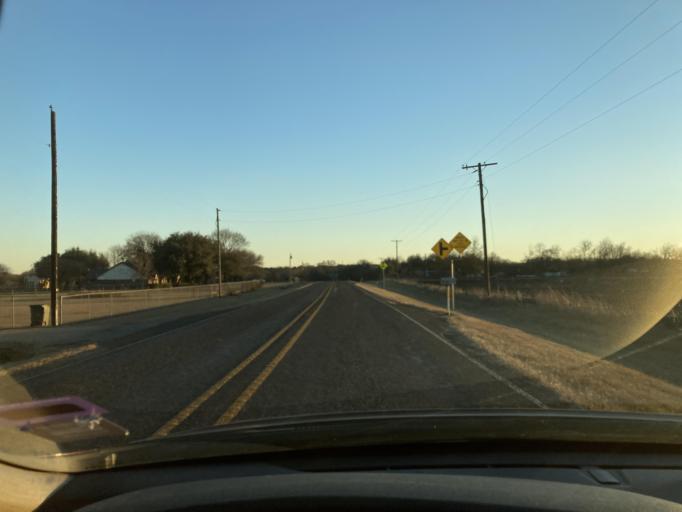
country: US
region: Texas
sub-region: Ellis County
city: Waxahachie
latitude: 32.3535
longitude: -96.8702
